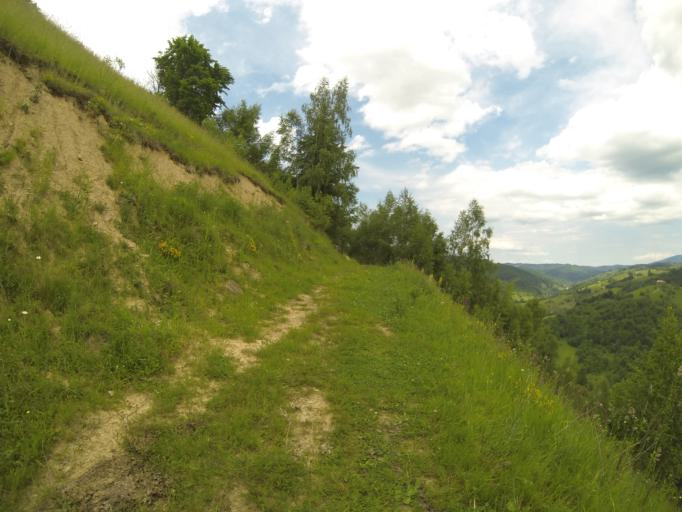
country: RO
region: Brasov
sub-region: Comuna Poiana Marului
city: Poiana Marului
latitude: 45.6481
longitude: 25.2879
